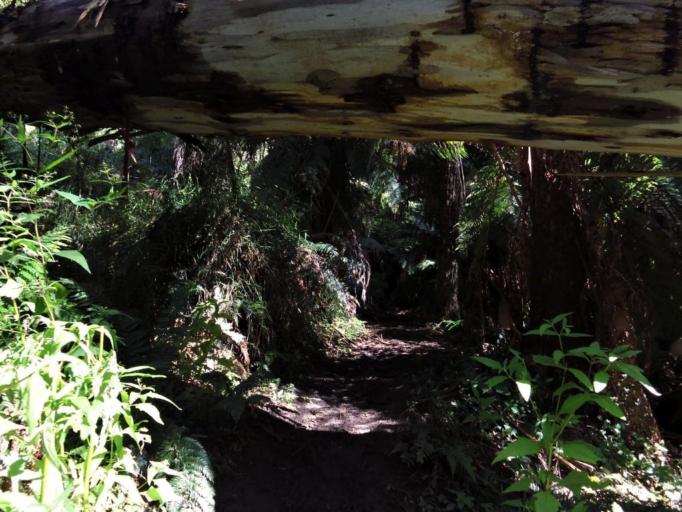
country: AU
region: Victoria
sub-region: Yarra Ranges
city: Millgrove
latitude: -37.7625
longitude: 145.6807
